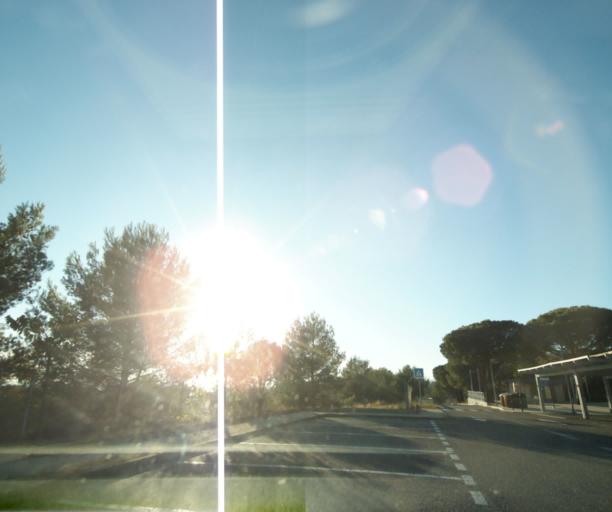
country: FR
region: Provence-Alpes-Cote d'Azur
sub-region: Departement des Bouches-du-Rhone
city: Ceyreste
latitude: 43.1937
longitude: 5.6679
